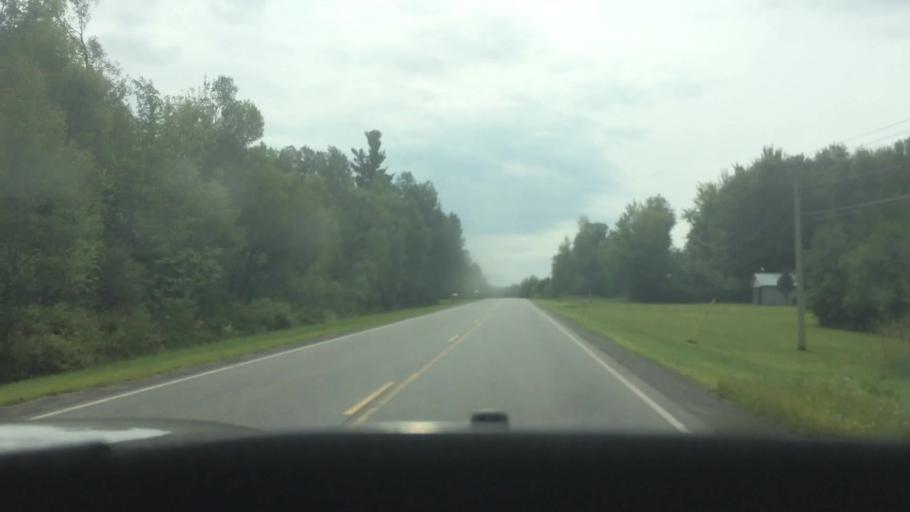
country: US
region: New York
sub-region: St. Lawrence County
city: Canton
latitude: 44.4988
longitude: -75.2657
